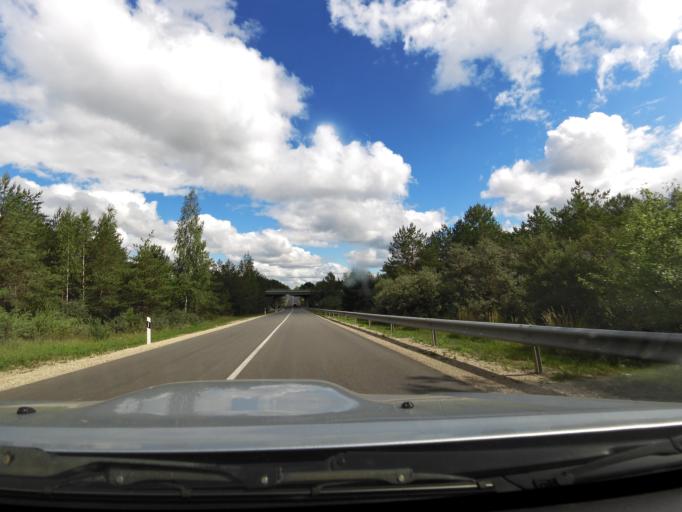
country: LT
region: Vilnius County
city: Ukmerge
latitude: 55.3322
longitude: 24.8892
